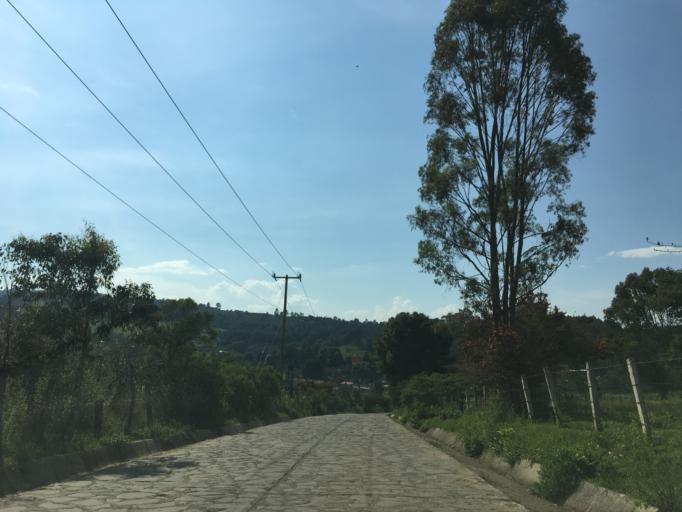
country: MX
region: Michoacan
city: Acuitzio del Canje
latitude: 19.5291
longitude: -101.2490
